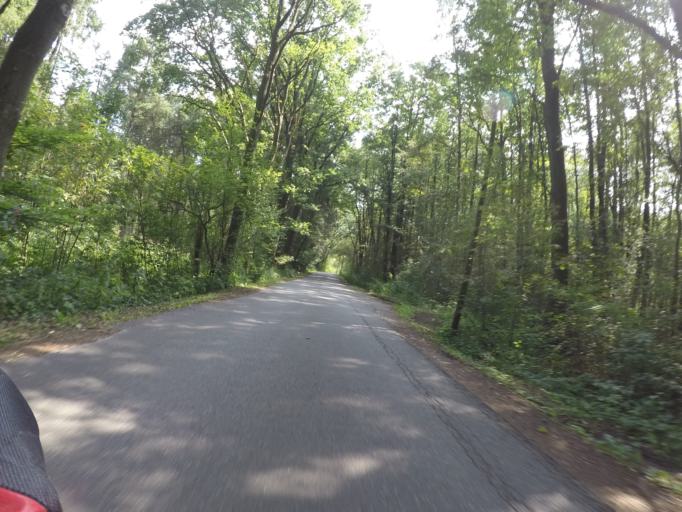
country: DE
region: Schleswig-Holstein
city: Tangstedt
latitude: 53.7549
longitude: 10.0442
